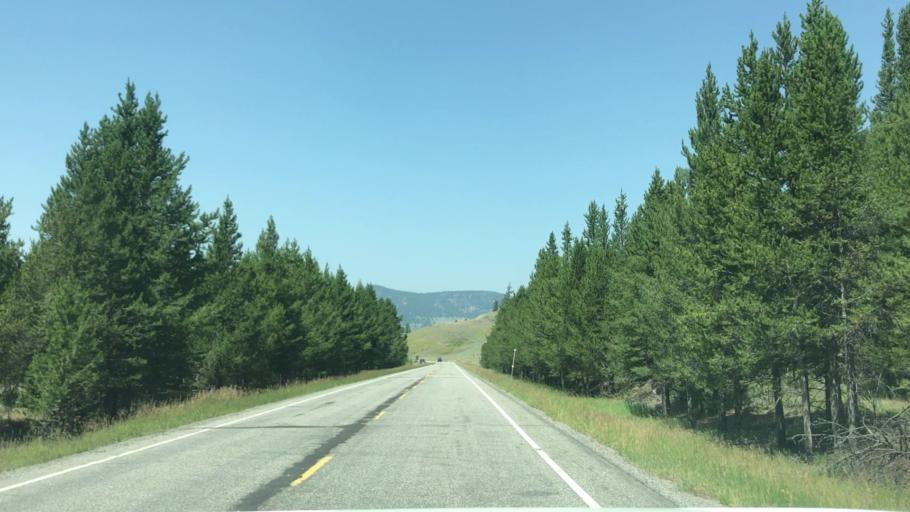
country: US
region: Montana
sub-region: Gallatin County
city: Big Sky
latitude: 45.0353
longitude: -111.1148
